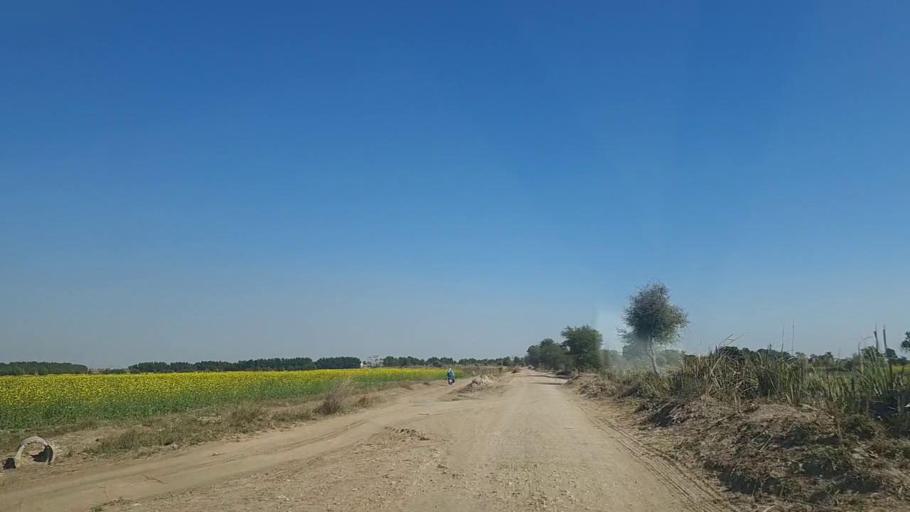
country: PK
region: Sindh
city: Sanghar
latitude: 26.2092
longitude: 68.9032
